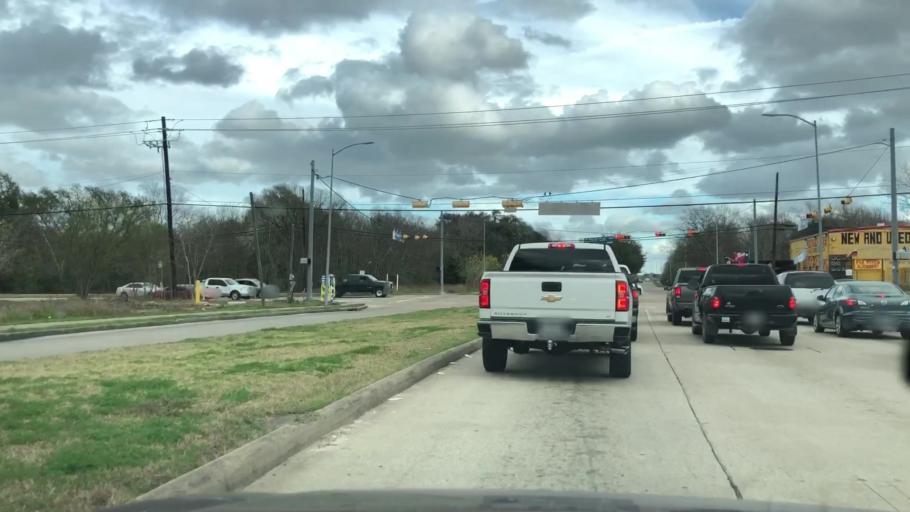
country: US
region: Texas
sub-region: Fort Bend County
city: Missouri City
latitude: 29.6122
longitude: -95.4657
